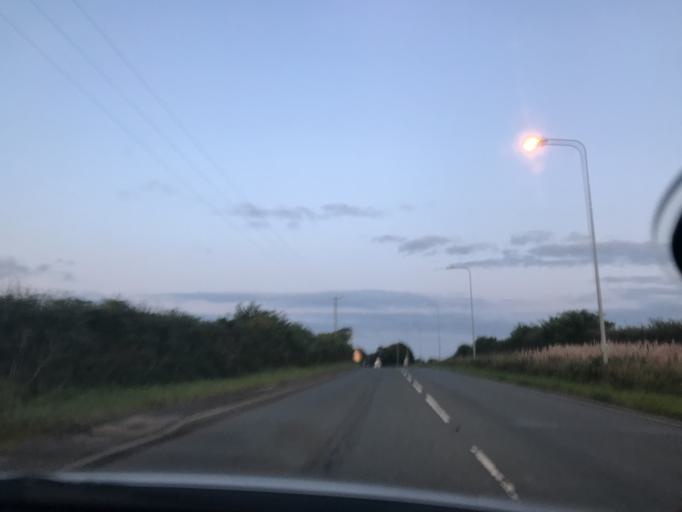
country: GB
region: England
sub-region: Cheshire West and Chester
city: Kelsall
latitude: 53.2113
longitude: -2.6770
